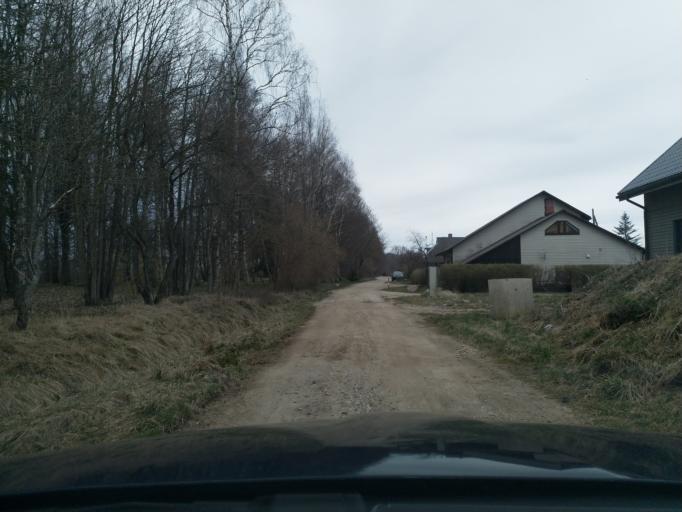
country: LV
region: Kuldigas Rajons
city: Kuldiga
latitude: 56.9549
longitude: 21.9998
